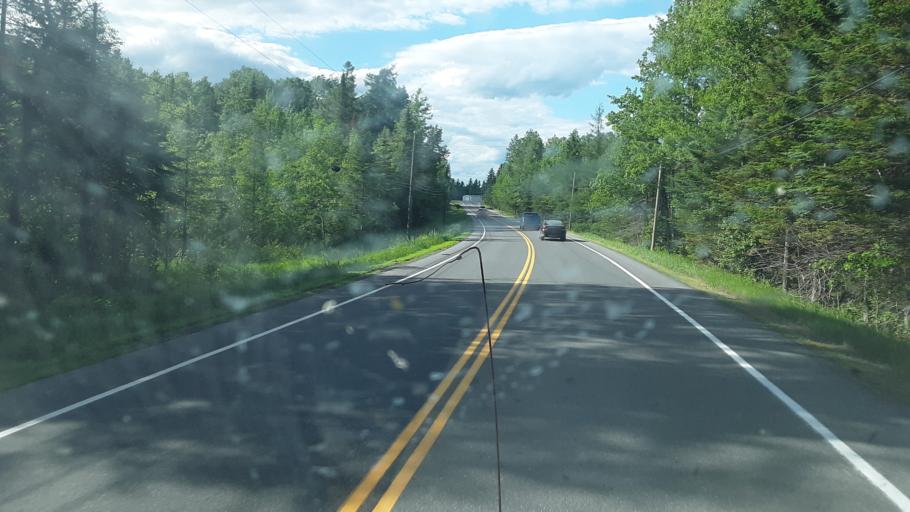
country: US
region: Maine
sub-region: Penobscot County
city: Patten
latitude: 45.9213
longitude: -68.4372
